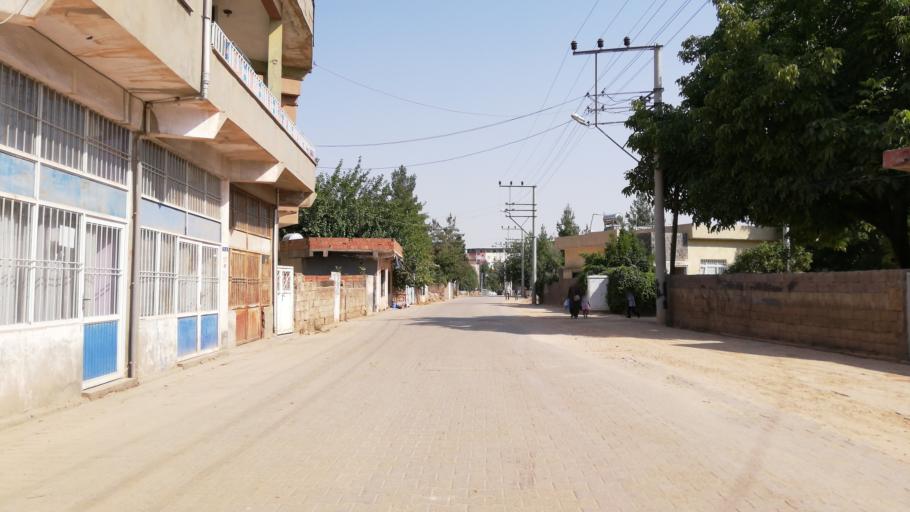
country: TR
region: Mardin
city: Midyat
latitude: 37.4269
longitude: 41.3421
